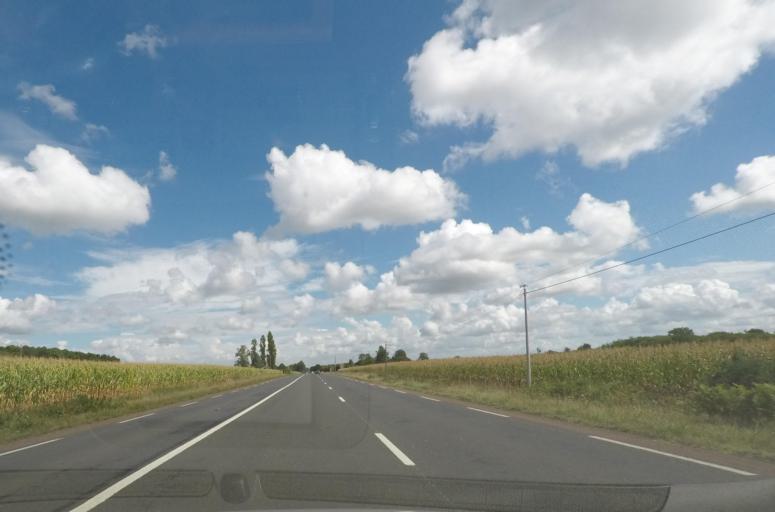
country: FR
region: Pays de la Loire
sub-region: Departement de la Sarthe
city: Clermont-Creans
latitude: 47.7692
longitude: 0.0222
